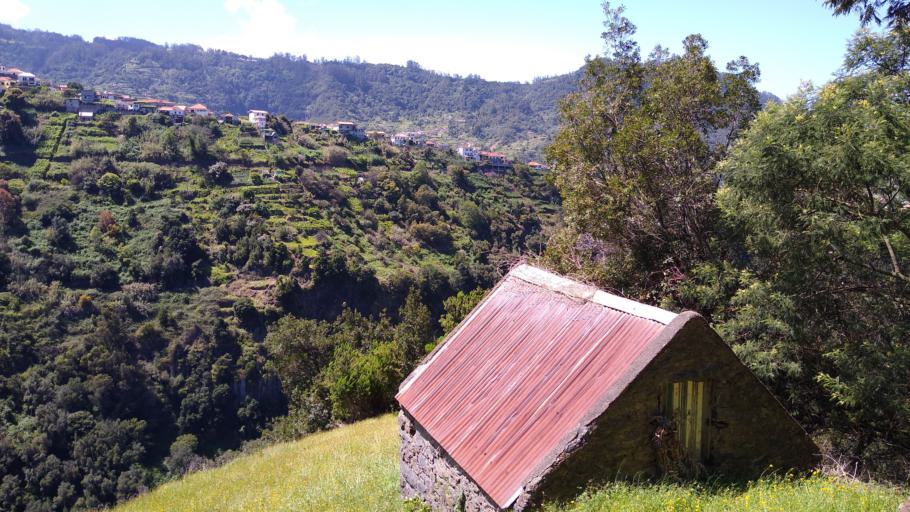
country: PT
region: Madeira
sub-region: Santana
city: Santana
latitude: 32.7651
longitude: -16.8530
